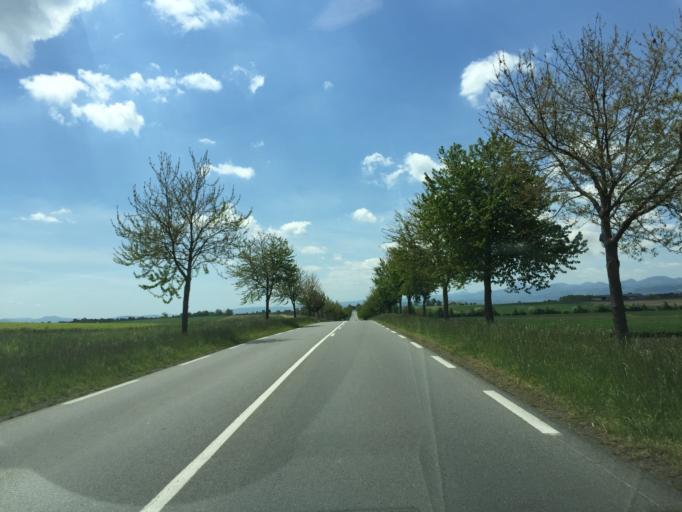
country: FR
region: Auvergne
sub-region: Departement du Puy-de-Dome
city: Aigueperse
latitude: 45.9922
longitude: 3.1884
